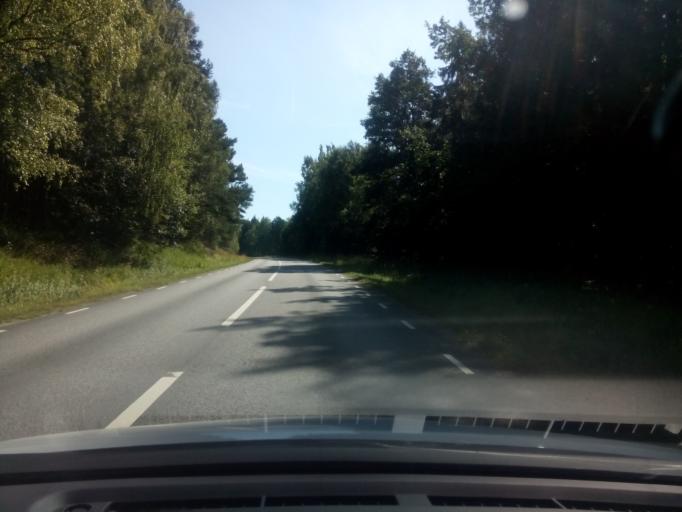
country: SE
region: Soedermanland
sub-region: Oxelosunds Kommun
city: Oxelosund
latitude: 58.7396
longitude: 17.2040
